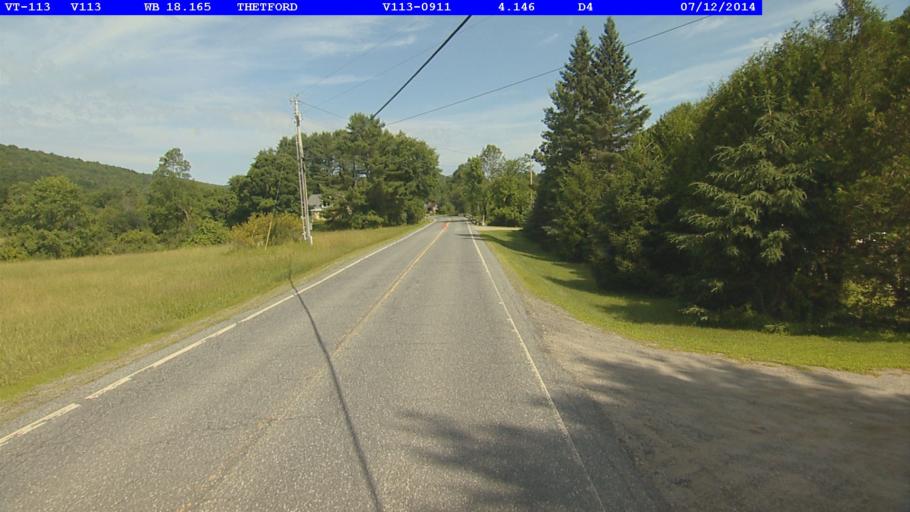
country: US
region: New Hampshire
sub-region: Grafton County
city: Lyme
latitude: 43.8419
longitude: -72.2477
